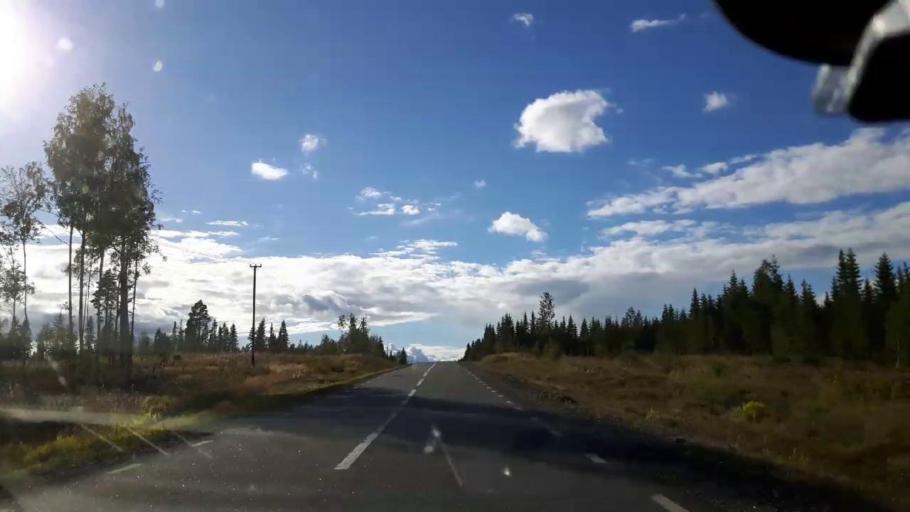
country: SE
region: Jaemtland
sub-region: Stroemsunds Kommun
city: Stroemsund
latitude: 63.5421
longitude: 15.9423
